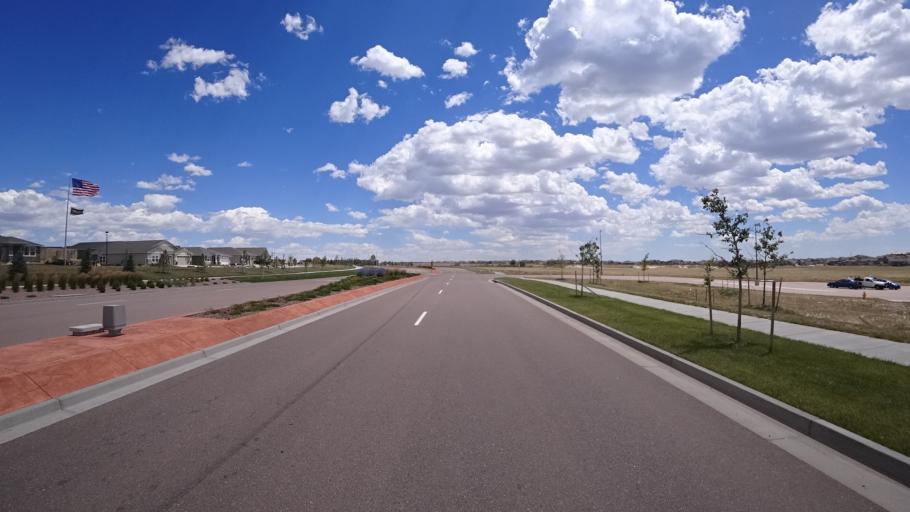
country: US
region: Colorado
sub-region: El Paso County
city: Black Forest
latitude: 38.9586
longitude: -104.7060
